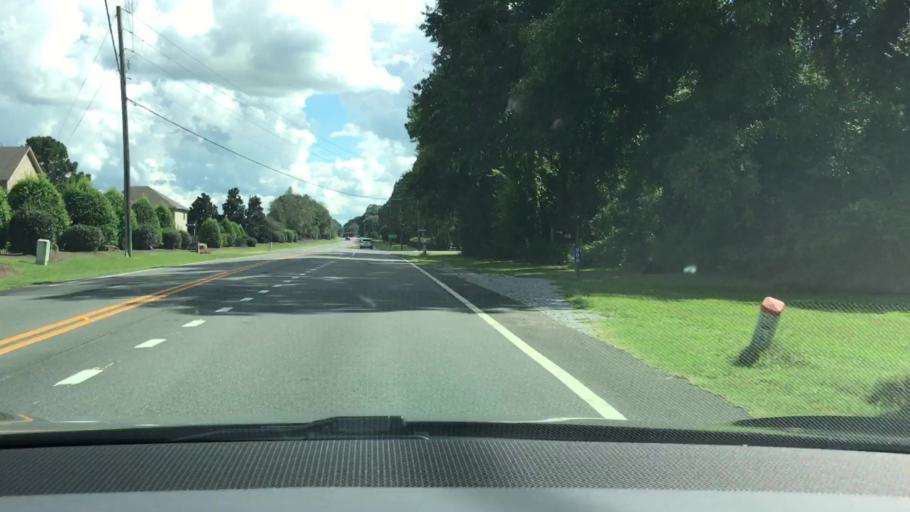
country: US
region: Alabama
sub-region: Montgomery County
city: Pike Road
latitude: 32.3550
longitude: -86.0950
